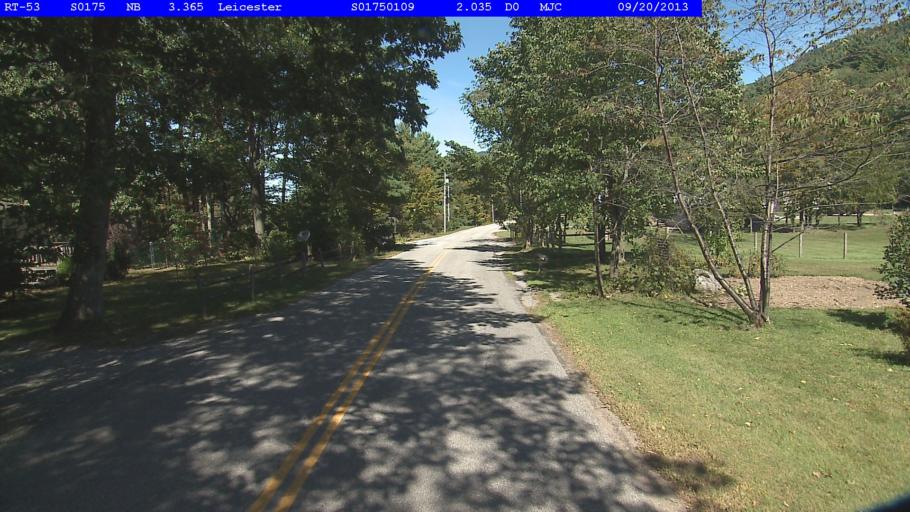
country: US
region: Vermont
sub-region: Rutland County
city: Brandon
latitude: 43.8722
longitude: -73.0646
